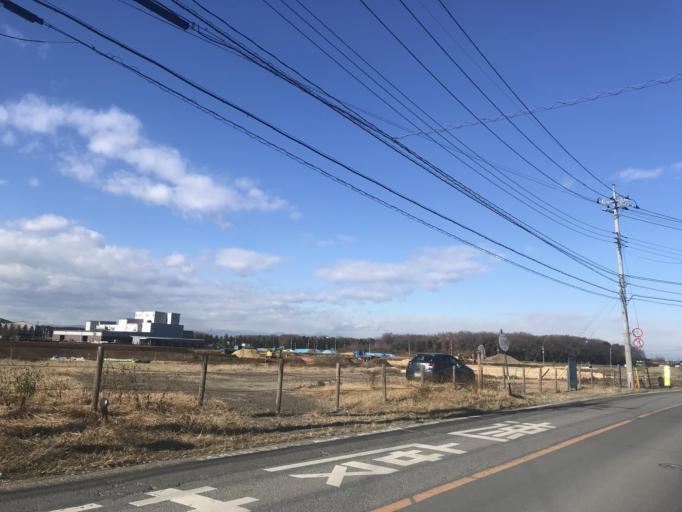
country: JP
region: Ibaraki
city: Yuki
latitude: 36.3625
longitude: 139.8767
